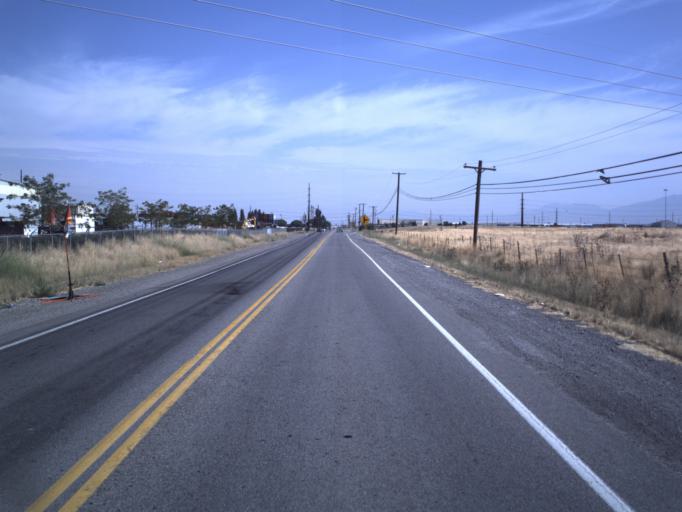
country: US
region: Utah
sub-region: Salt Lake County
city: West Valley City
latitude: 40.7432
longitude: -112.0249
